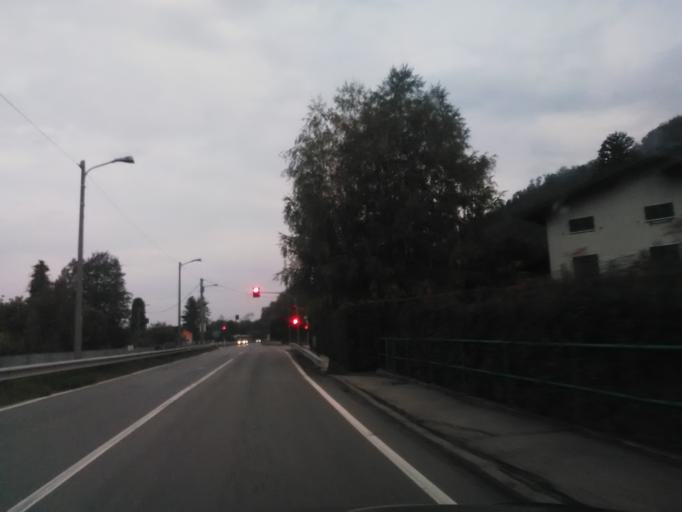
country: IT
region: Piedmont
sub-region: Provincia di Vercelli
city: Serravalle Sesia
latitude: 45.6949
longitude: 8.2973
